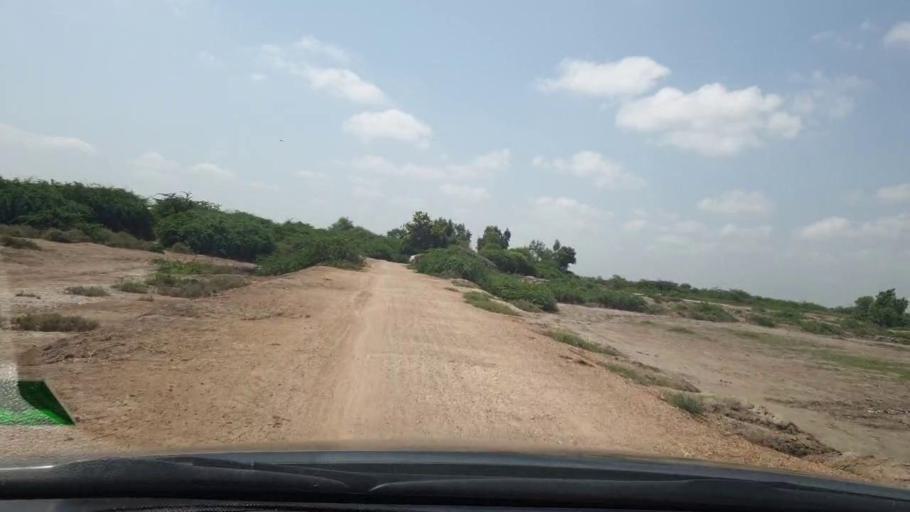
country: PK
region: Sindh
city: Tando Bago
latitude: 24.8587
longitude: 69.0871
